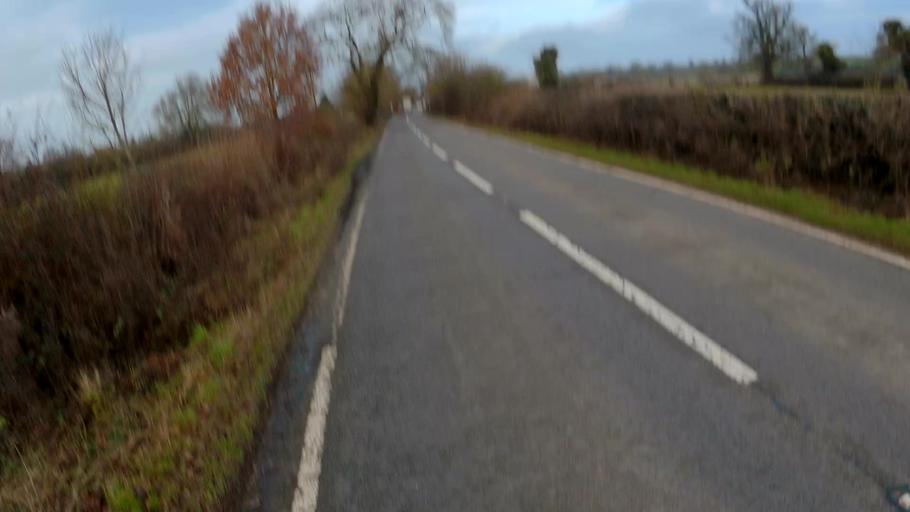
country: GB
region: England
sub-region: Lincolnshire
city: Bourne
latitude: 52.7773
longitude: -0.4262
